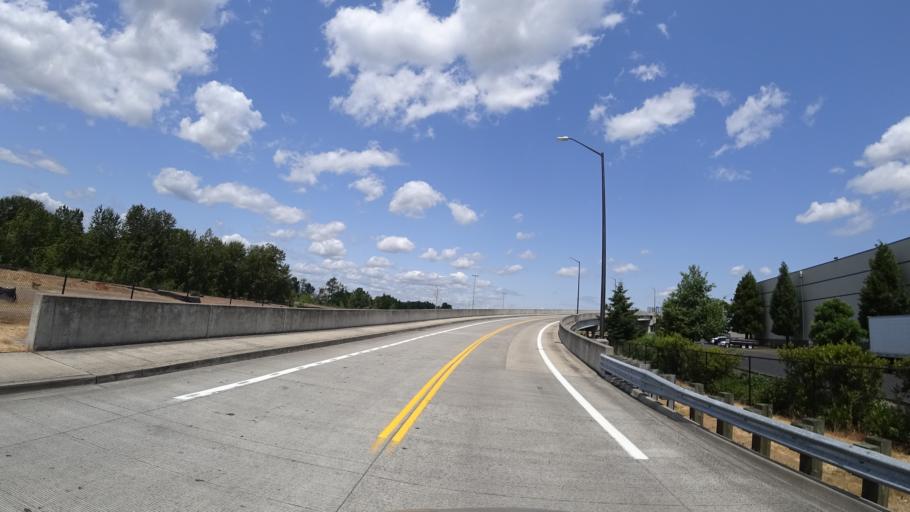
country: US
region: Washington
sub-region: Clark County
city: Lake Shore
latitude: 45.6333
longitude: -122.7574
